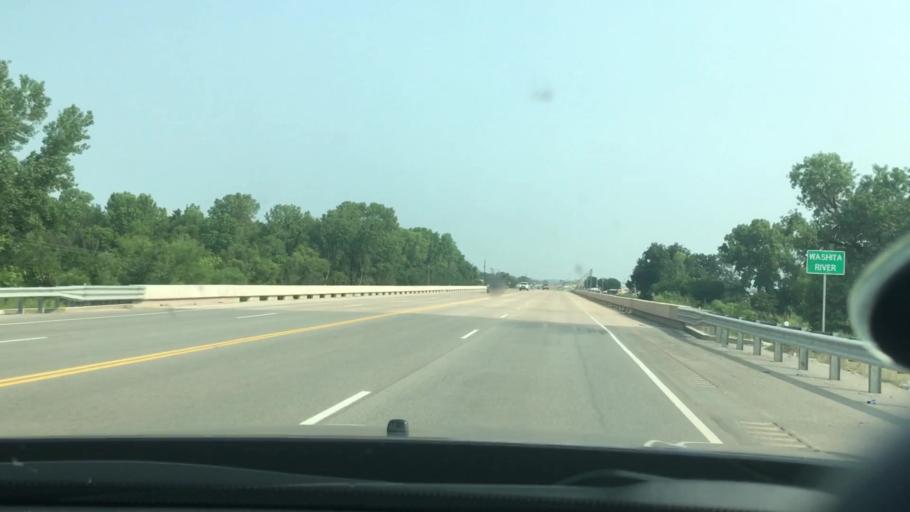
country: US
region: Oklahoma
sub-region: Garvin County
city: Lindsay
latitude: 34.8171
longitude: -97.5981
